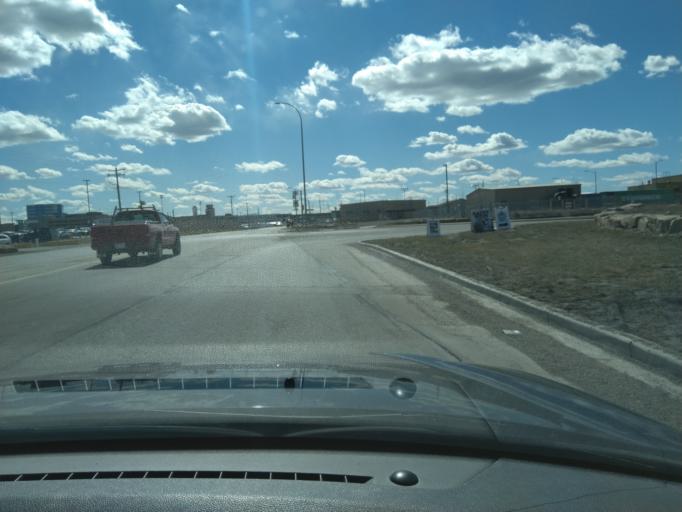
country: CA
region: Alberta
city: Calgary
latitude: 51.1380
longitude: -114.0134
